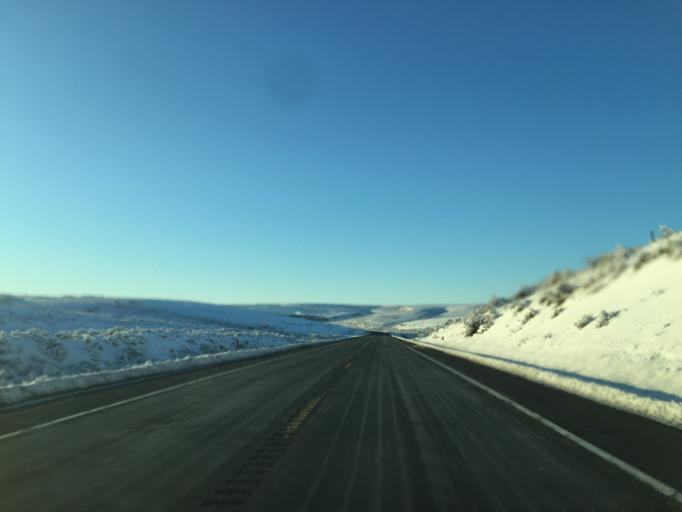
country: US
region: Washington
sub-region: Grant County
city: Soap Lake
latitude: 47.6050
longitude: -119.6353
